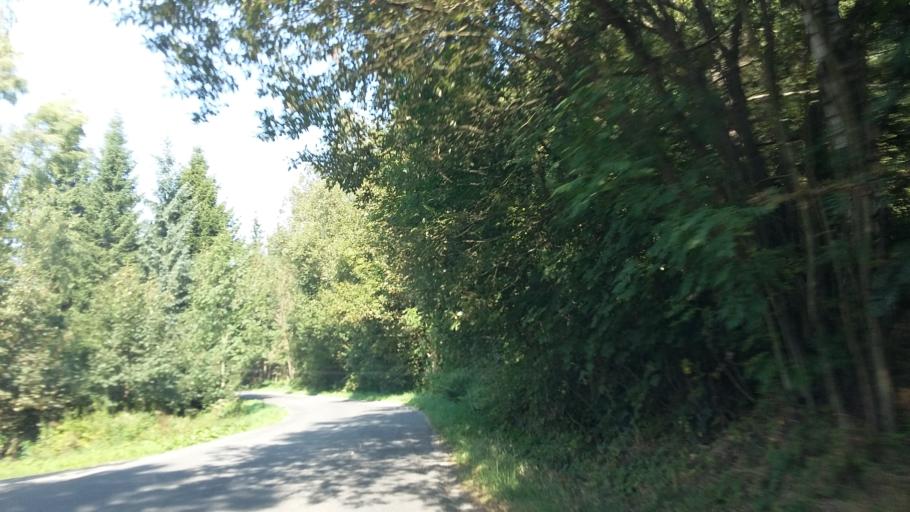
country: CZ
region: Liberecky
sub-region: Okres Jablonec nad Nisou
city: Janov nad Nisou
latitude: 50.7694
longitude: 15.1900
